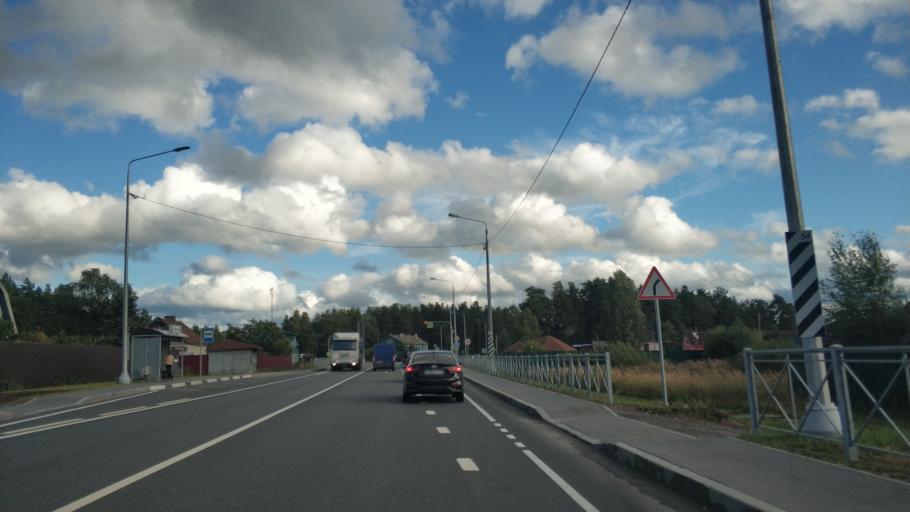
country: RU
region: Leningrad
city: Priozersk
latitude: 61.0065
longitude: 30.1773
